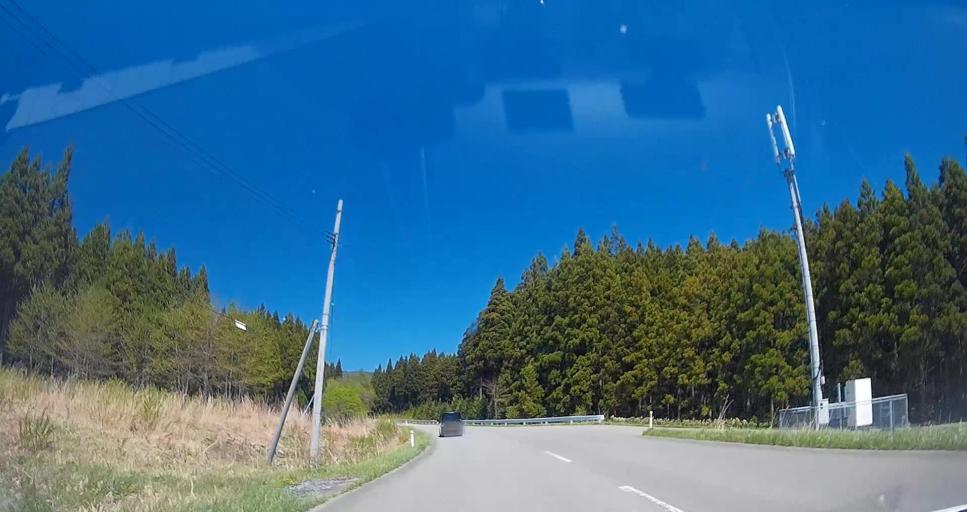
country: JP
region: Aomori
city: Mutsu
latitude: 41.2953
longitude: 141.3965
